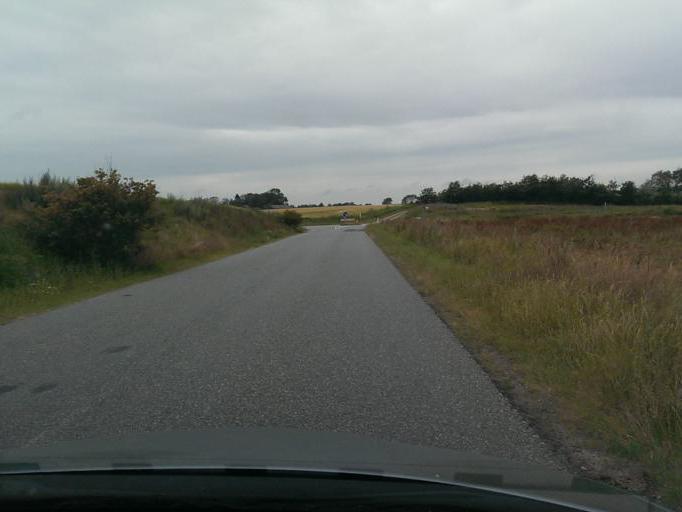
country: DK
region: North Denmark
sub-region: Hjorring Kommune
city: Vra
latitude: 57.3566
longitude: 9.9266
